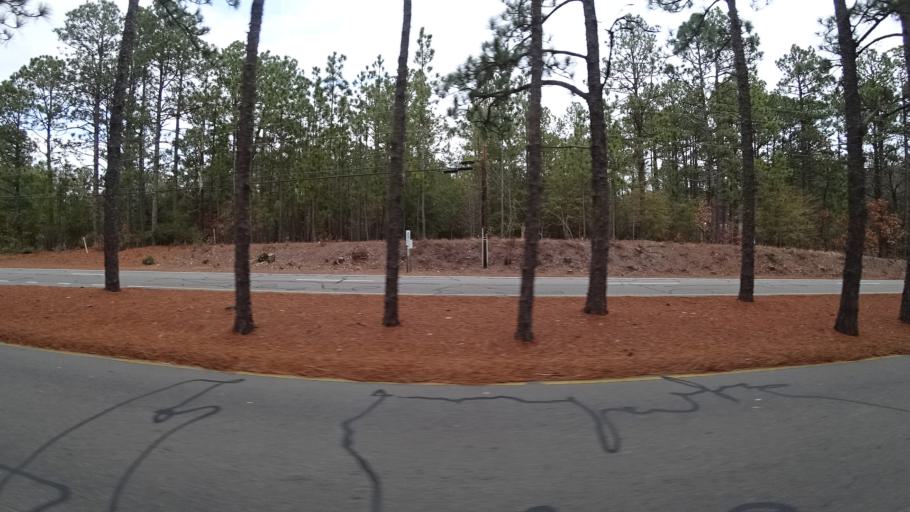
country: US
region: North Carolina
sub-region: Moore County
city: Pinehurst
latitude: 35.2010
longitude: -79.4307
